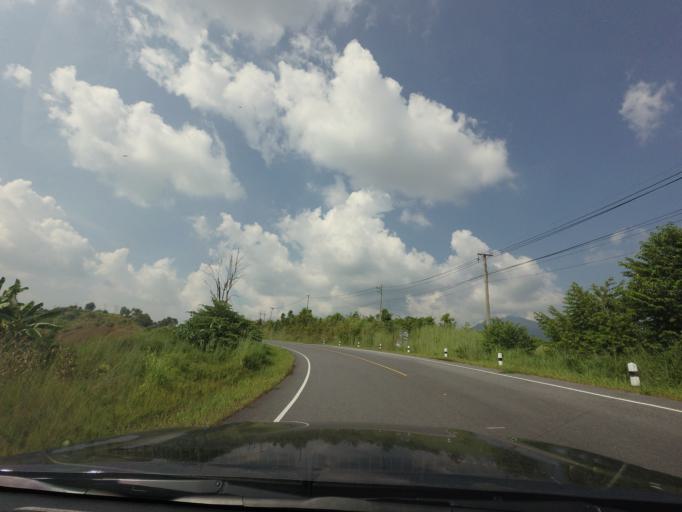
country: TH
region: Nan
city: Santi Suk
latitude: 18.9784
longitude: 100.9672
